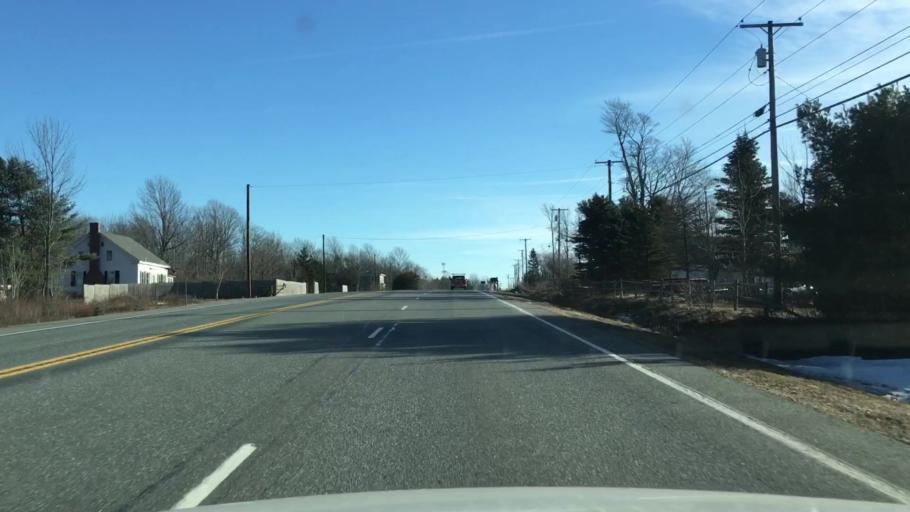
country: US
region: Maine
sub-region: Hancock County
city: Surry
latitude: 44.6265
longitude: -68.5358
